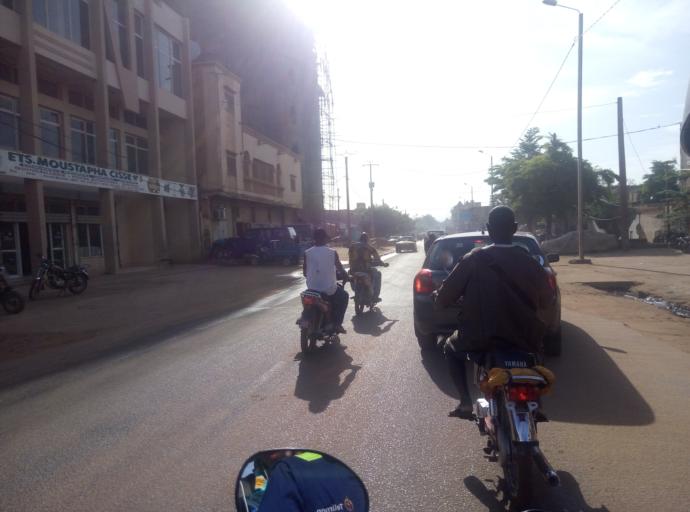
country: ML
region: Bamako
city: Bamako
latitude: 12.6421
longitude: -7.9860
